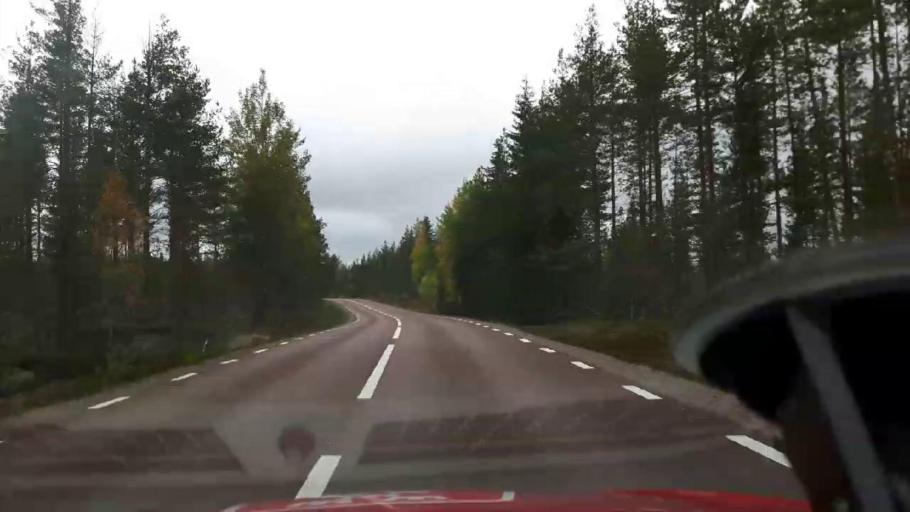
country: SE
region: Jaemtland
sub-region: Harjedalens Kommun
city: Sveg
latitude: 62.2101
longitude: 14.8447
